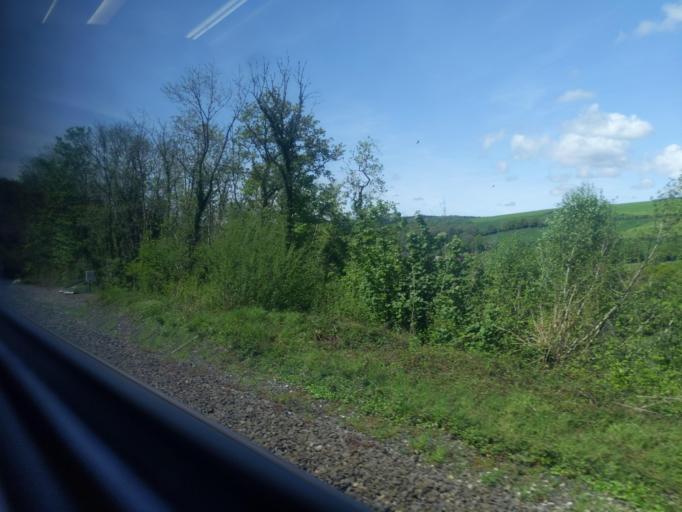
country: GB
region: England
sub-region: Cornwall
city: Lostwithiel
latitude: 50.4546
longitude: -4.5878
